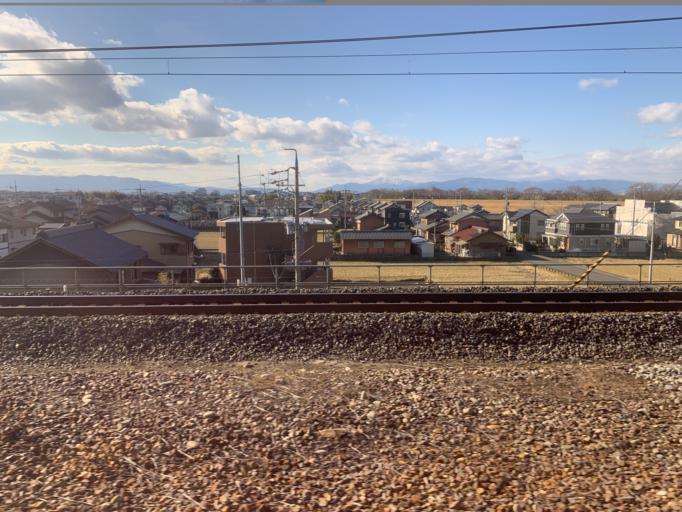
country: JP
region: Gifu
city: Kasamatsucho
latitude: 35.3663
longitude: 136.7799
